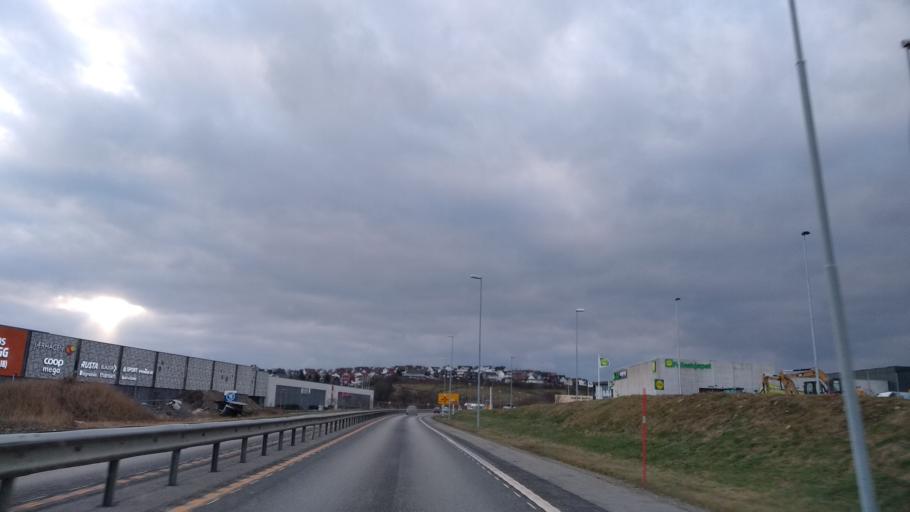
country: NO
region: Rogaland
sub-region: Klepp
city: Kleppe
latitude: 58.7822
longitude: 5.6268
